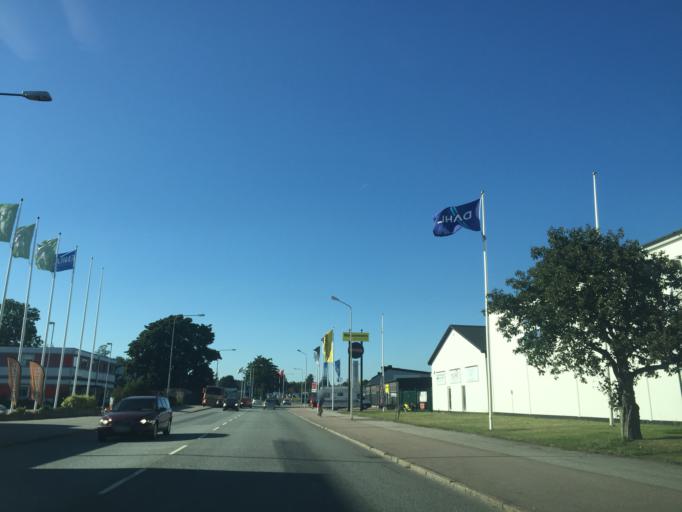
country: SE
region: Skane
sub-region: Ystads Kommun
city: Ystad
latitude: 55.4364
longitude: 13.8372
